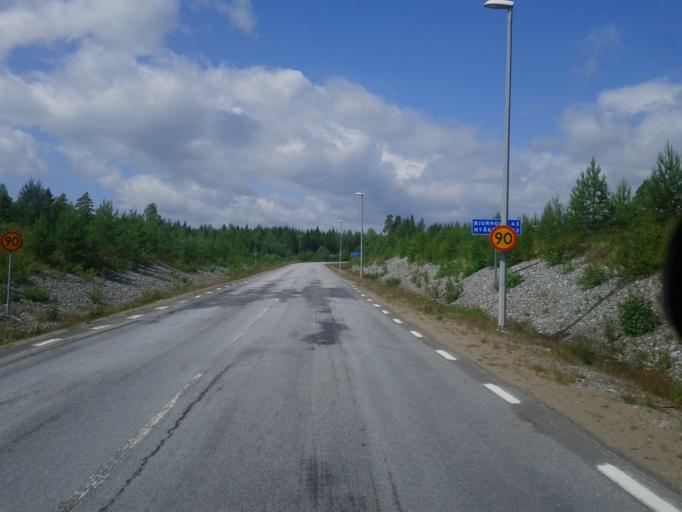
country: SE
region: Vaesterbotten
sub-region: Nordmalings Kommun
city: Nordmaling
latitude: 63.5789
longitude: 19.4613
